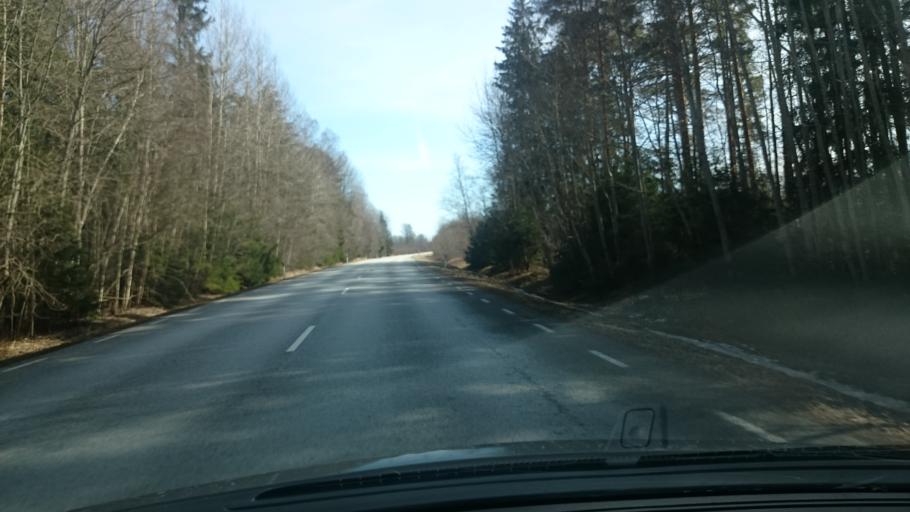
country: EE
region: Paernumaa
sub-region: Tootsi vald
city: Tootsi
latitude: 58.6625
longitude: 24.8180
